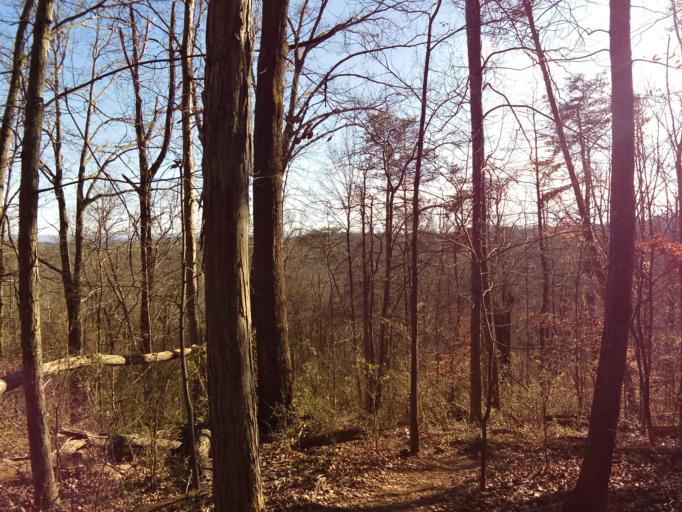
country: US
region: Tennessee
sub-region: Knox County
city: Knoxville
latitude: 35.9501
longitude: -83.8716
